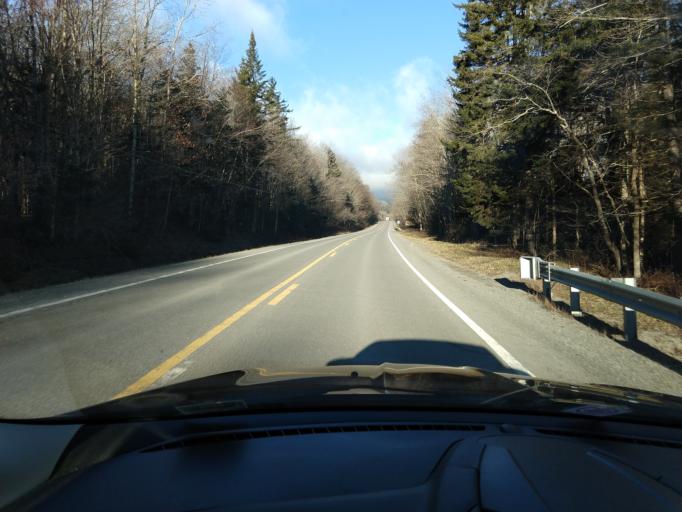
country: US
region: West Virginia
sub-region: Randolph County
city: Elkins
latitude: 38.6022
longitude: -79.8569
